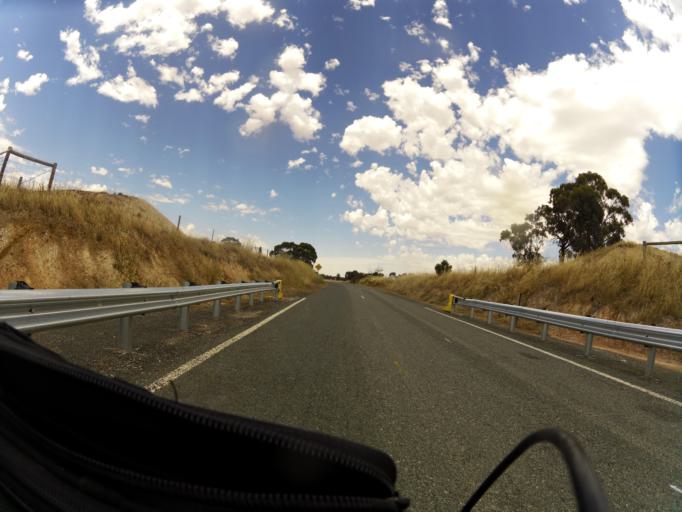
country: AU
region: Victoria
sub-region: Greater Shepparton
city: Shepparton
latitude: -36.6312
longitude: 145.2107
